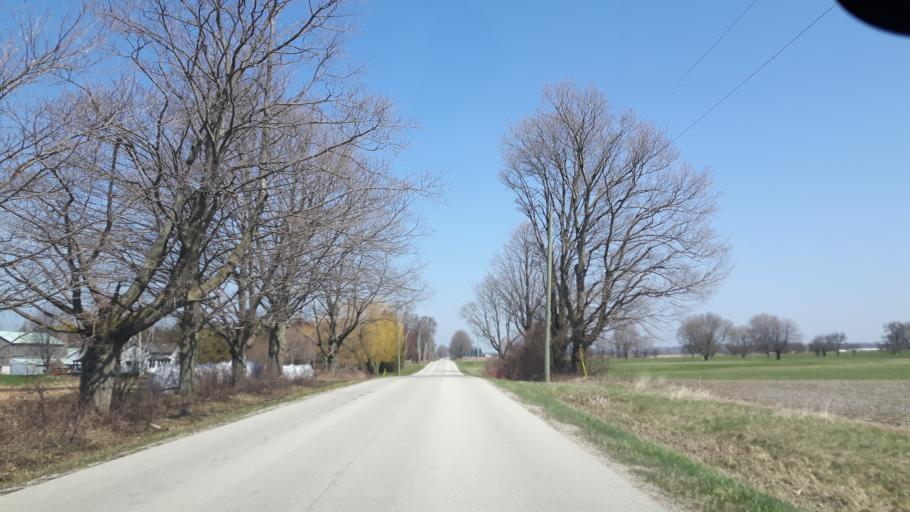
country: CA
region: Ontario
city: Goderich
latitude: 43.6281
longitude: -81.6846
